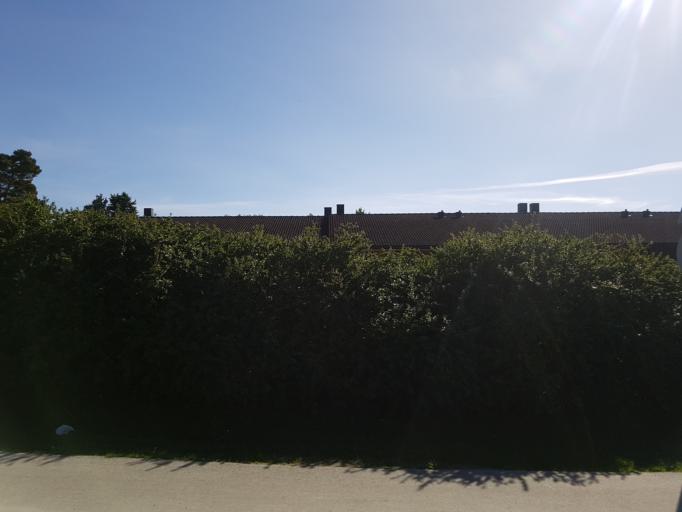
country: NO
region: Sor-Trondelag
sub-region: Trondheim
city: Trondheim
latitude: 63.4279
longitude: 10.4988
